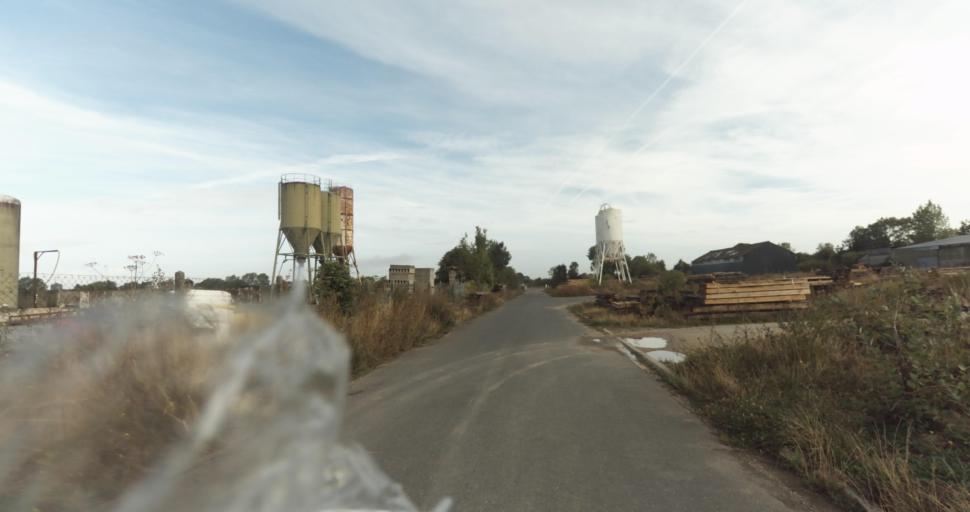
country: FR
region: Lower Normandy
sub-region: Departement de l'Orne
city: Gace
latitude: 48.8966
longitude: 0.3289
